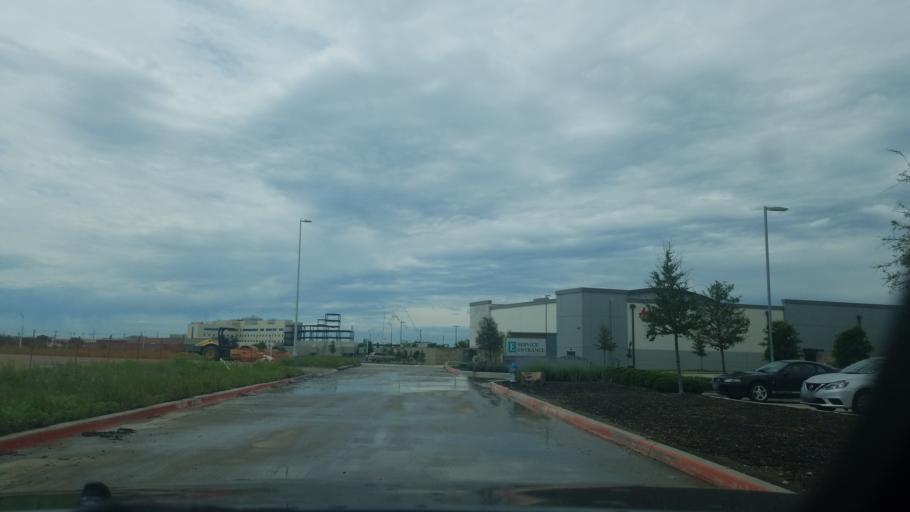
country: US
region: Texas
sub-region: Denton County
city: Denton
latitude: 33.2231
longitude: -97.1679
